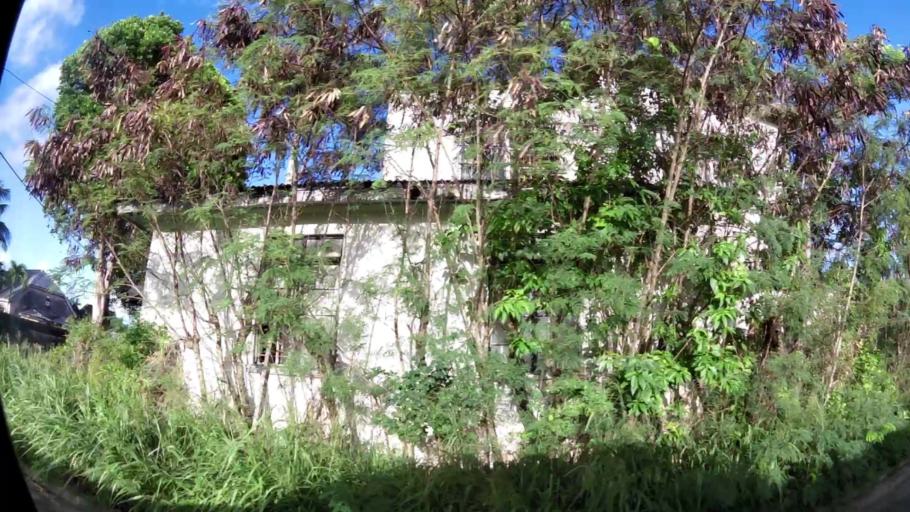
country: BB
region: Christ Church
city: Oistins
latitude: 13.0674
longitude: -59.5539
